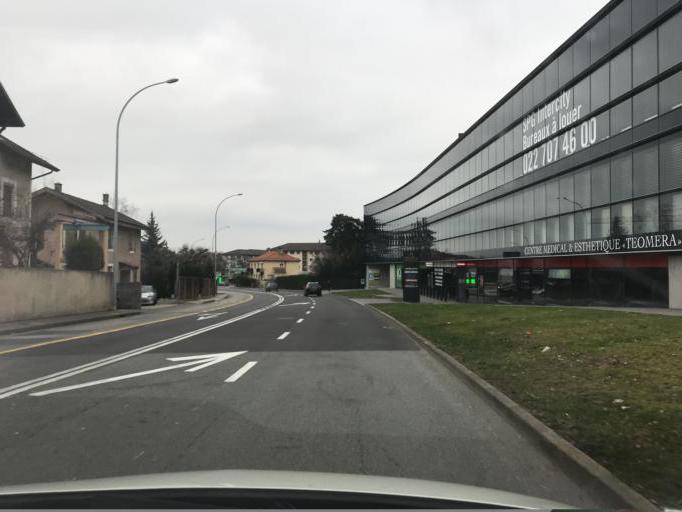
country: CH
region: Geneva
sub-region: Geneva
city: Le Grand-Saconnex
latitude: 46.2343
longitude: 6.1238
